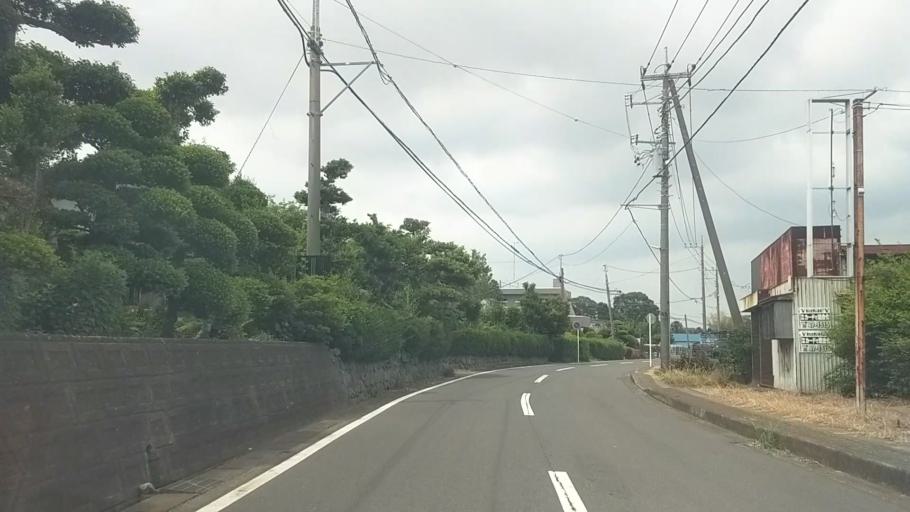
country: JP
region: Kanagawa
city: Chigasaki
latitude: 35.3891
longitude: 139.4142
